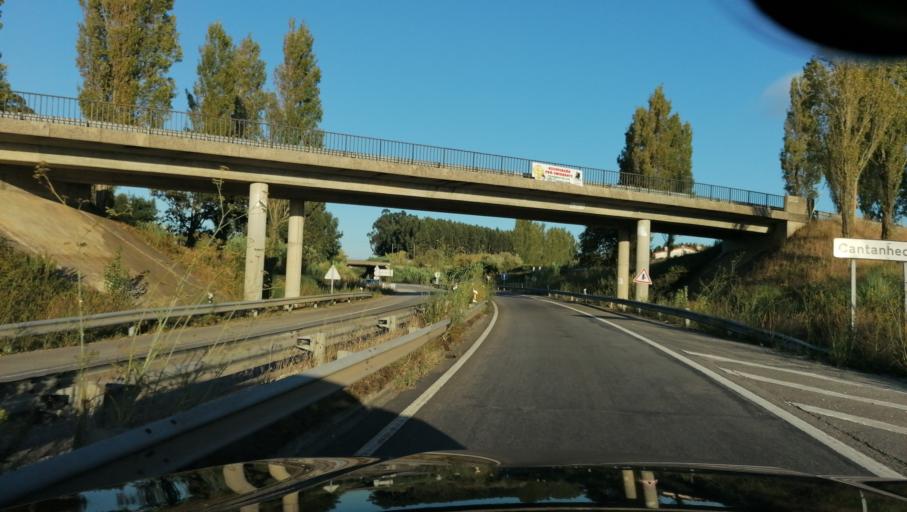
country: PT
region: Aveiro
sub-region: Aveiro
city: Aradas
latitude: 40.6114
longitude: -8.6315
